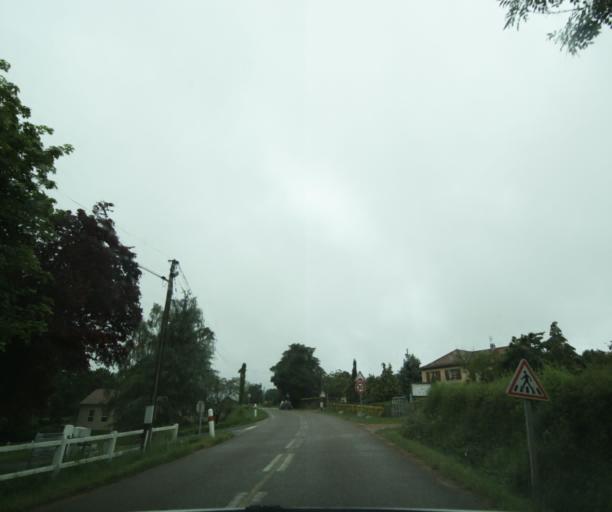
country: FR
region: Bourgogne
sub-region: Departement de Saone-et-Loire
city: Charolles
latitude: 46.4709
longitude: 4.2437
